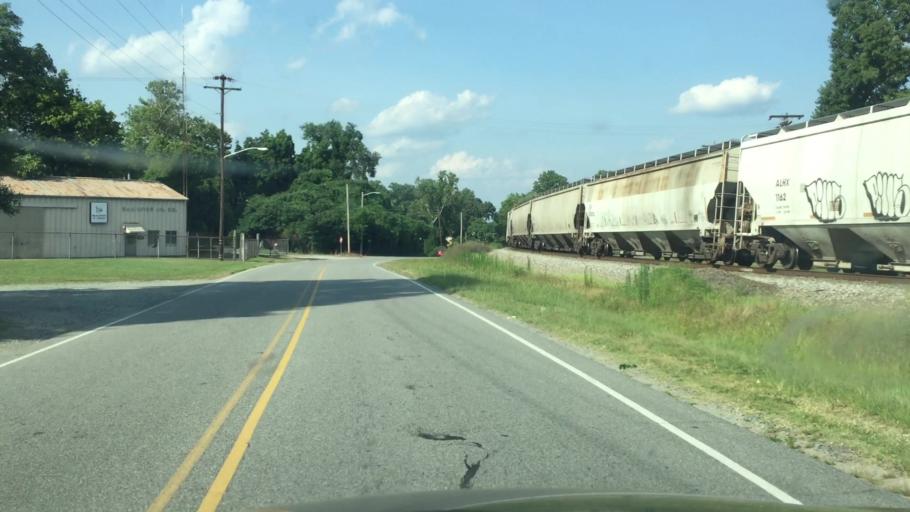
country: US
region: North Carolina
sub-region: Rockingham County
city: Reidsville
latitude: 36.3697
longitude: -79.6630
